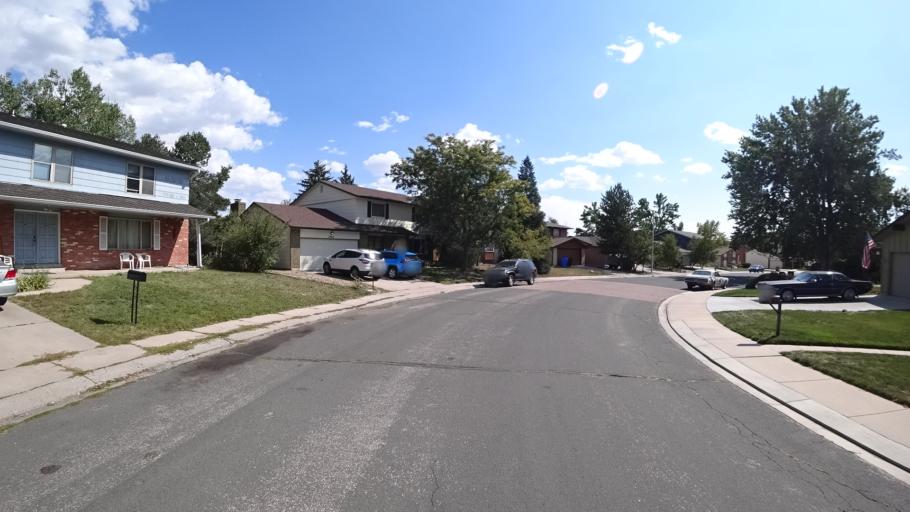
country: US
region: Colorado
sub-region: El Paso County
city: Cimarron Hills
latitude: 38.8743
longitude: -104.7506
